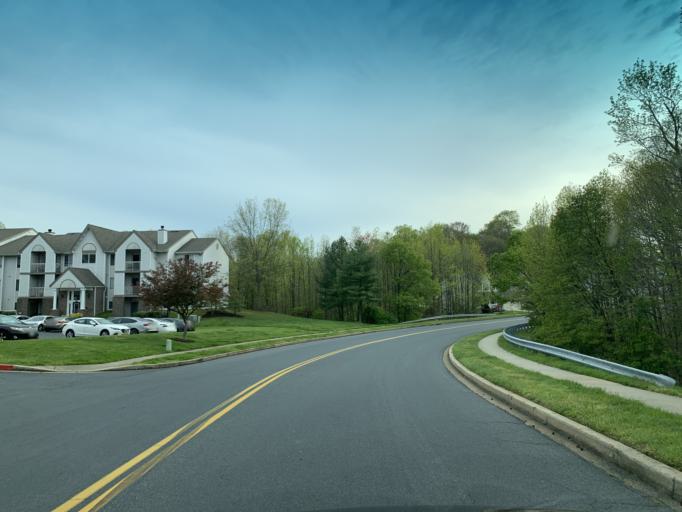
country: US
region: Maryland
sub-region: Harford County
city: Riverside
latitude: 39.4766
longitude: -76.2516
